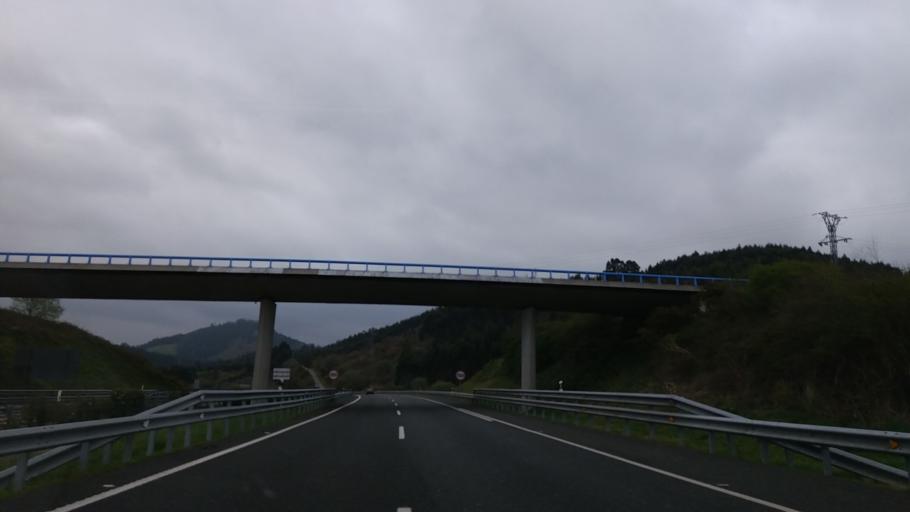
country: ES
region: Cantabria
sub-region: Provincia de Cantabria
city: San Vicente de la Barquera
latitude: 43.3610
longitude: -4.3960
